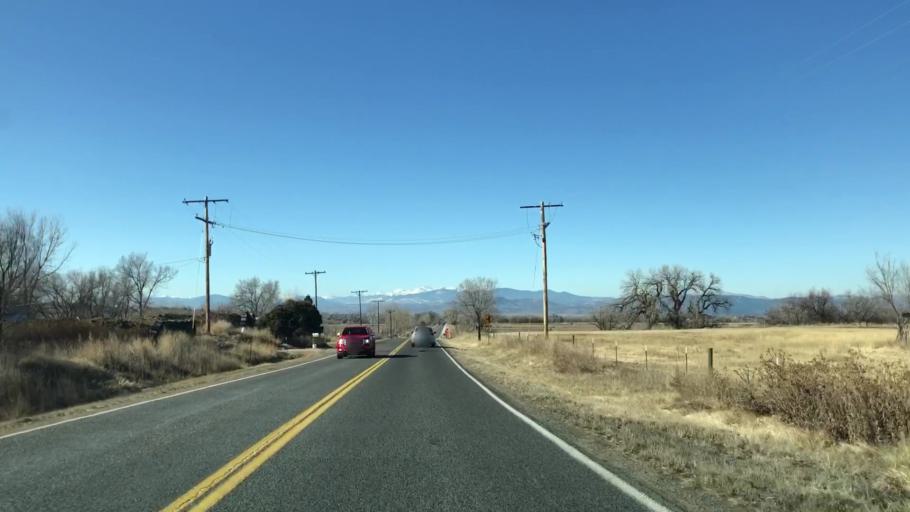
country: US
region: Colorado
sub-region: Weld County
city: Windsor
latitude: 40.4865
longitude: -104.9412
